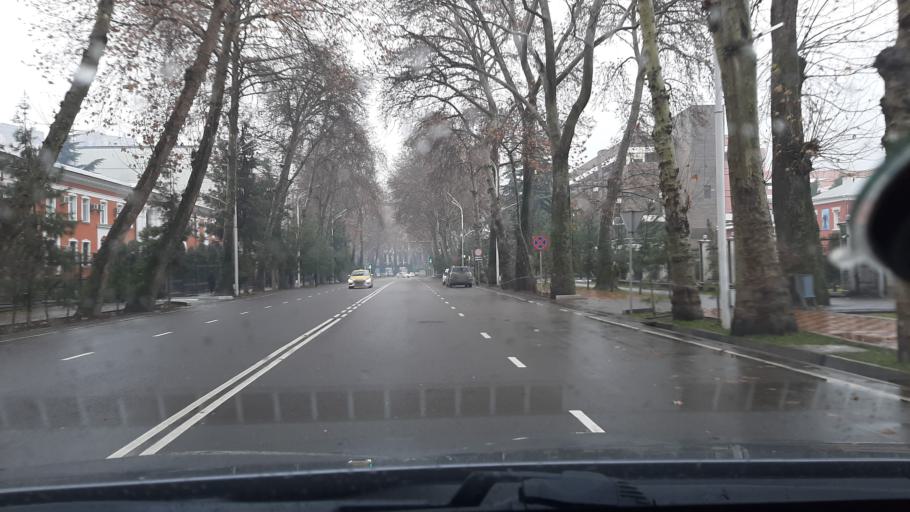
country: TJ
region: Dushanbe
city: Dushanbe
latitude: 38.5718
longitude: 68.7847
